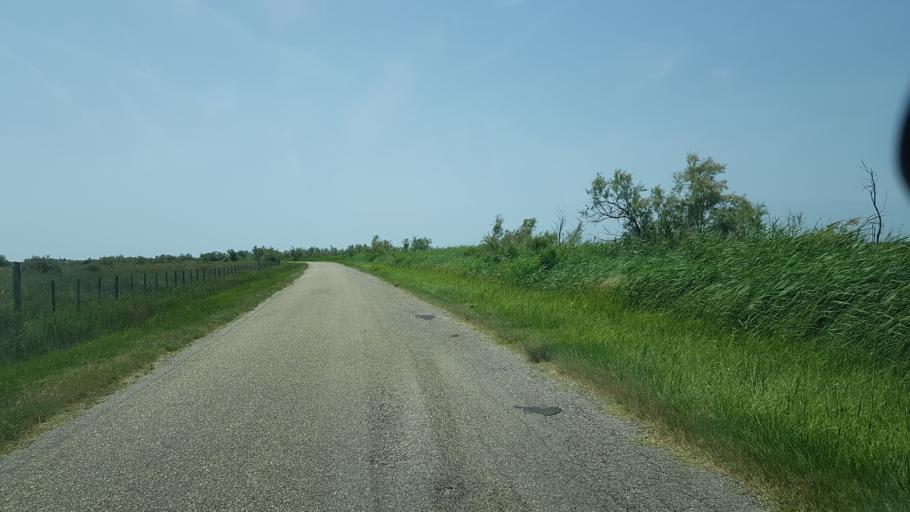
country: FR
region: Provence-Alpes-Cote d'Azur
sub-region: Departement des Bouches-du-Rhone
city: Arles
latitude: 43.4954
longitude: 4.6417
